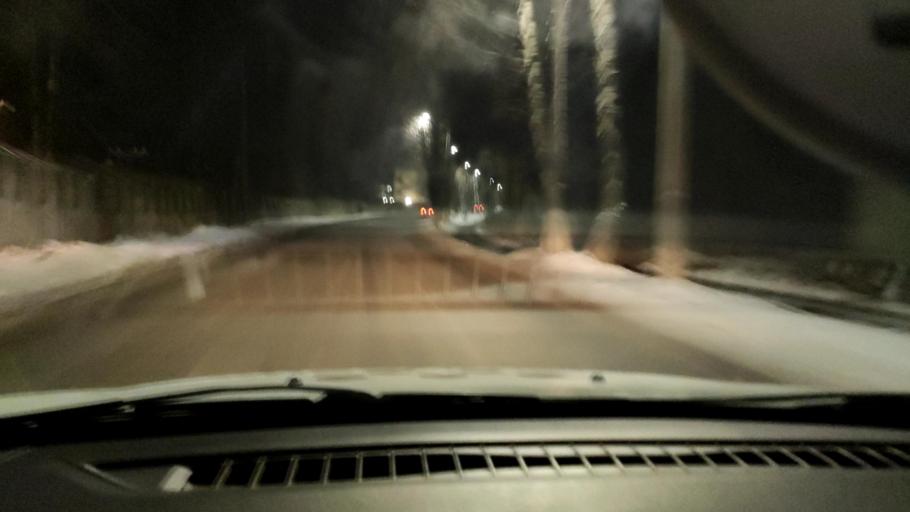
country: RU
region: Perm
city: Kultayevo
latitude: 57.9889
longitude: 55.9253
